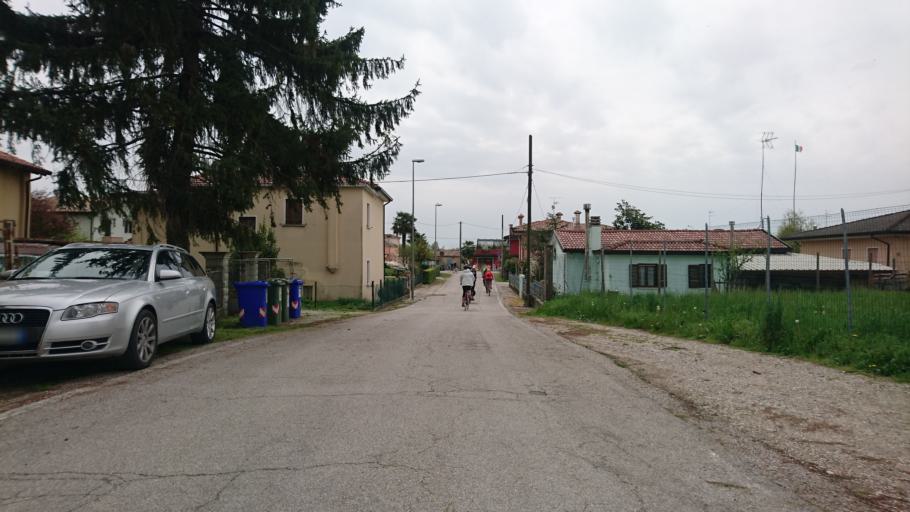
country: IT
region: Veneto
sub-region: Provincia di Venezia
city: Concordia Sagittaria
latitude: 45.7016
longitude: 12.8724
